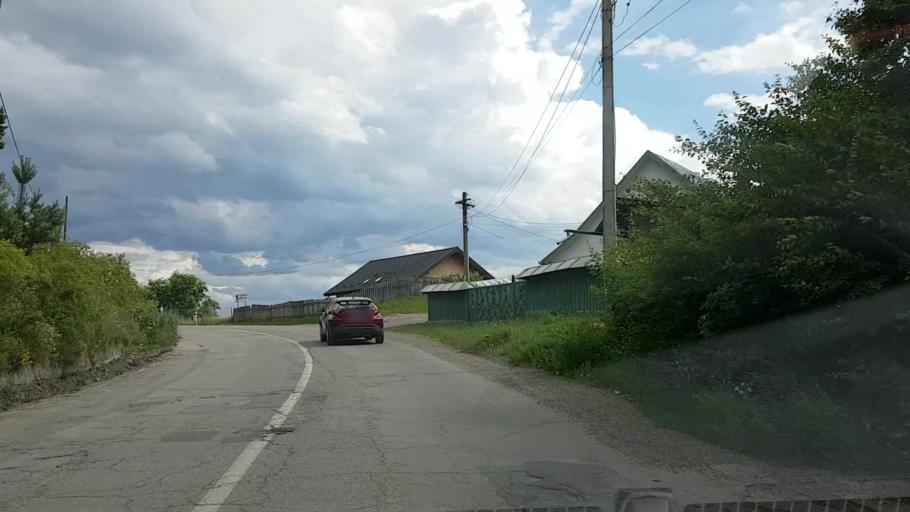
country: RO
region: Neamt
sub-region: Comuna Hangu
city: Hangu
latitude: 47.0478
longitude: 26.0396
